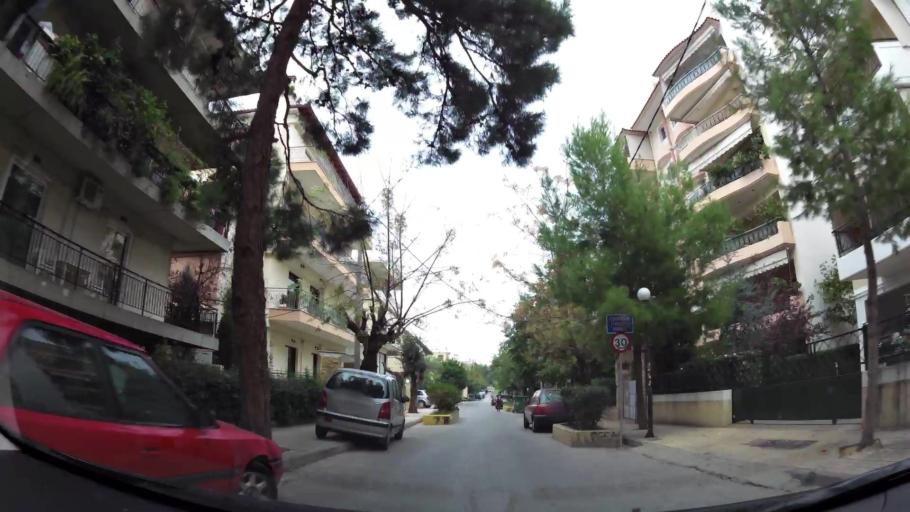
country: GR
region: Attica
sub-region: Nomarchia Athinas
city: Irakleio
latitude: 38.0414
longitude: 23.7692
